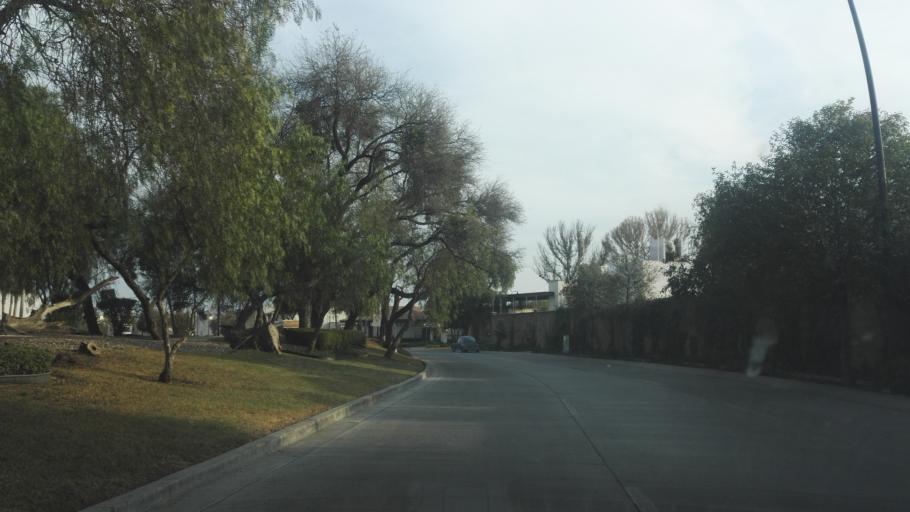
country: MX
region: Guanajuato
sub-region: Leon
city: Ladrilleras del Refugio
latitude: 21.0645
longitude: -101.5983
